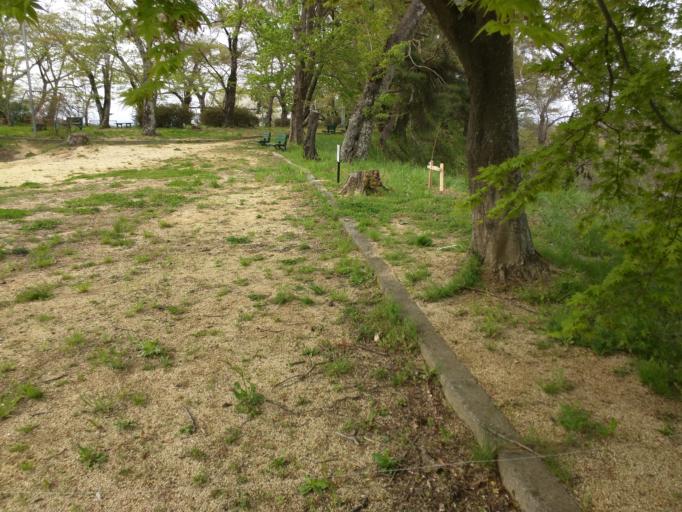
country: JP
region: Fukushima
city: Nihommatsu
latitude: 37.5638
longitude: 140.5124
